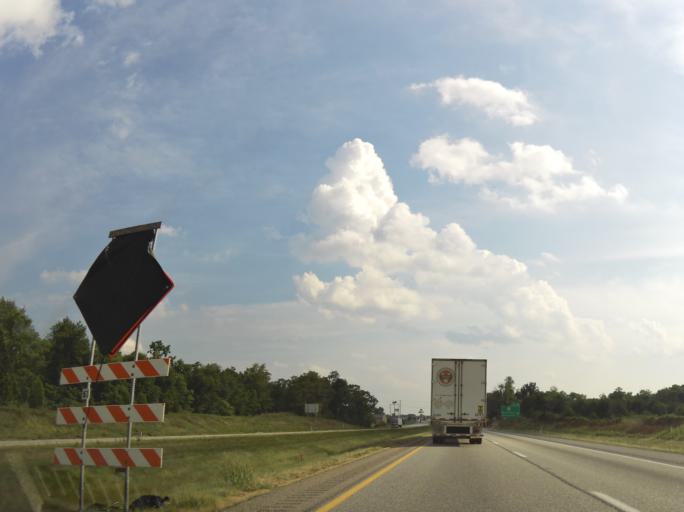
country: US
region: Pennsylvania
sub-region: Franklin County
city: Greencastle
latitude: 39.7934
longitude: -77.7115
